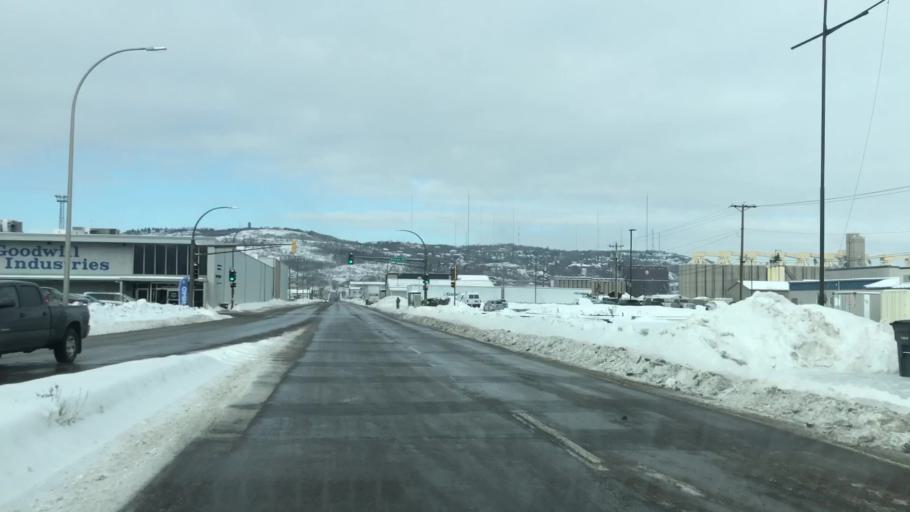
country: US
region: Minnesota
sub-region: Saint Louis County
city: Duluth
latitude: 46.7595
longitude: -92.1090
